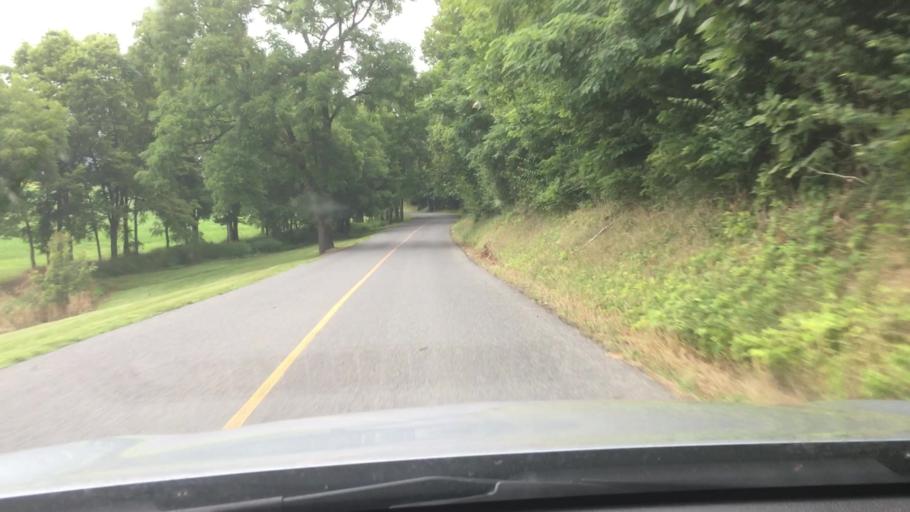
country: US
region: Pennsylvania
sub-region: Franklin County
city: Greencastle
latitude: 39.8618
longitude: -77.7994
